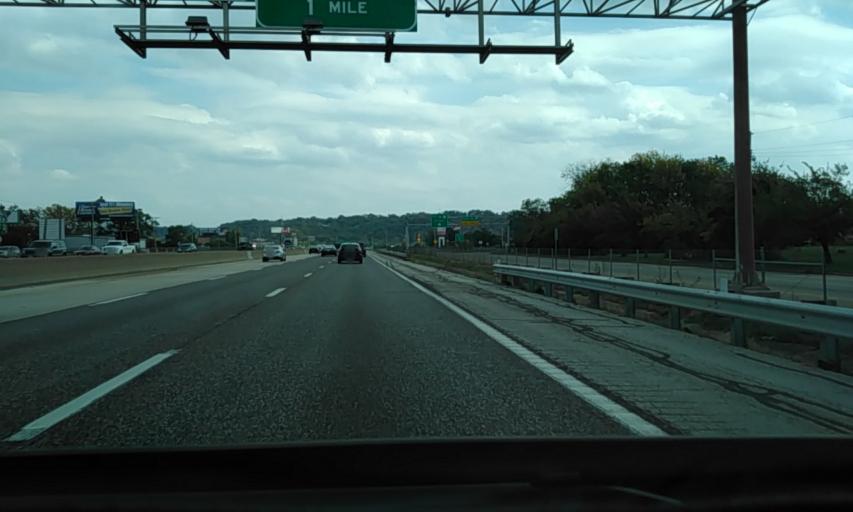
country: US
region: Missouri
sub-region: Saint Louis County
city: Fenton
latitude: 38.5427
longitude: -90.4487
